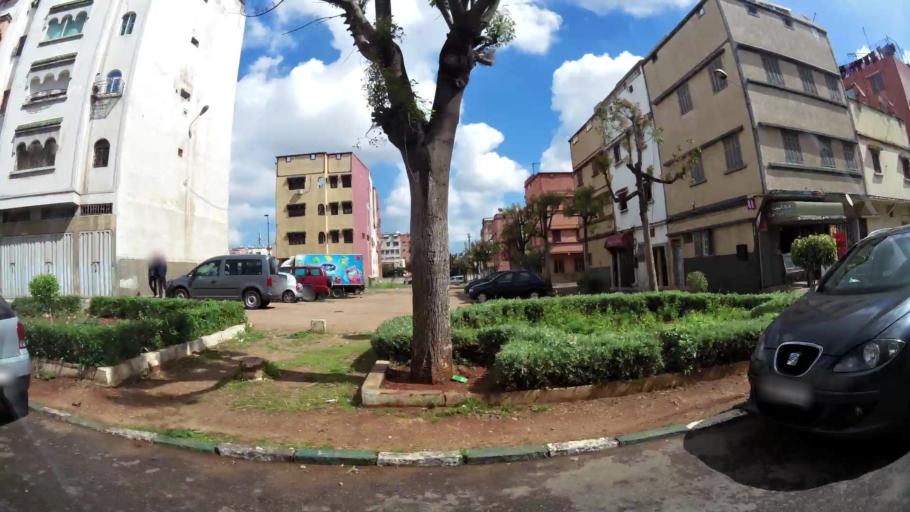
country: MA
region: Grand Casablanca
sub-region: Casablanca
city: Casablanca
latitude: 33.5495
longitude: -7.6019
